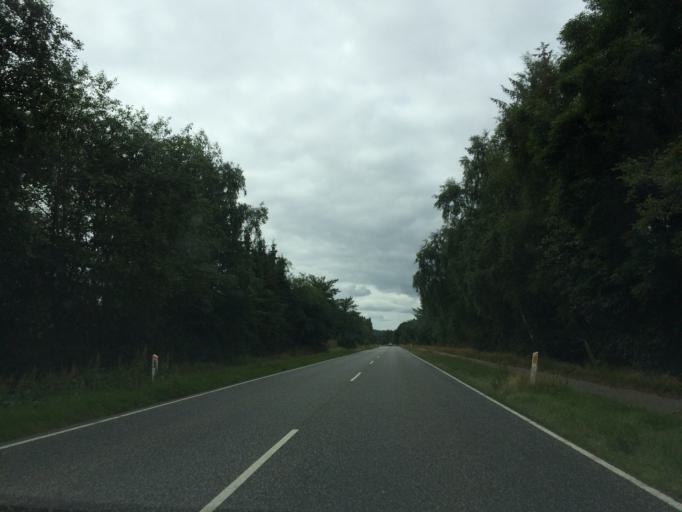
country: DK
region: Central Jutland
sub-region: Silkeborg Kommune
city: Svejbaek
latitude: 56.1759
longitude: 9.6232
